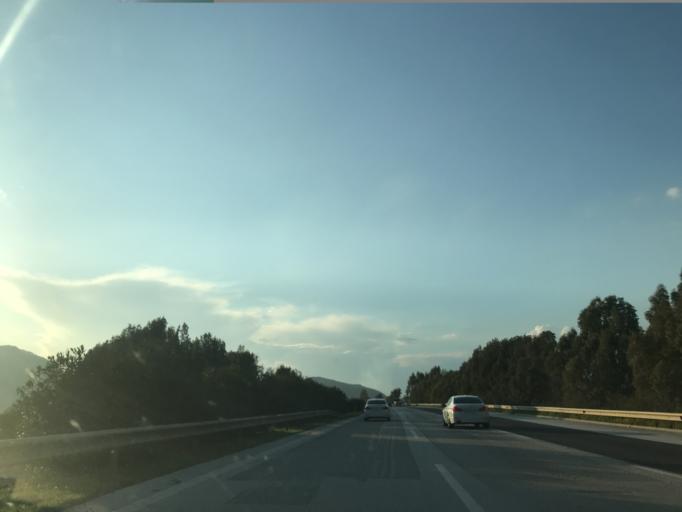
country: TR
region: Adana
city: Ceyhan
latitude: 36.9839
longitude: 35.7724
